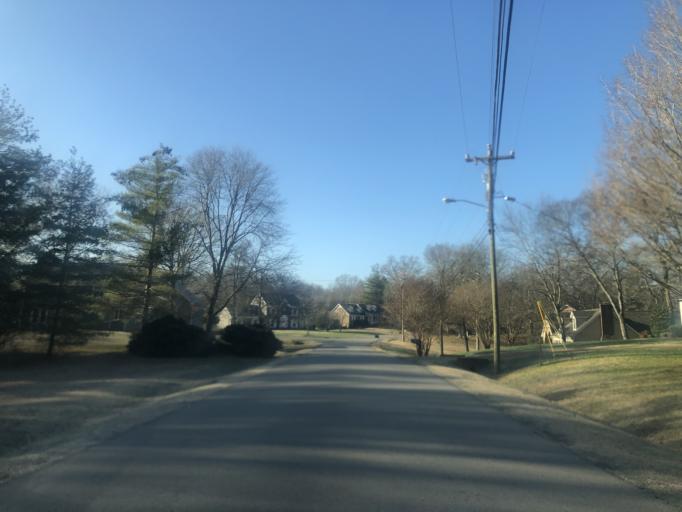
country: US
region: Tennessee
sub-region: Williamson County
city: Brentwood Estates
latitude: 36.0025
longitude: -86.7180
